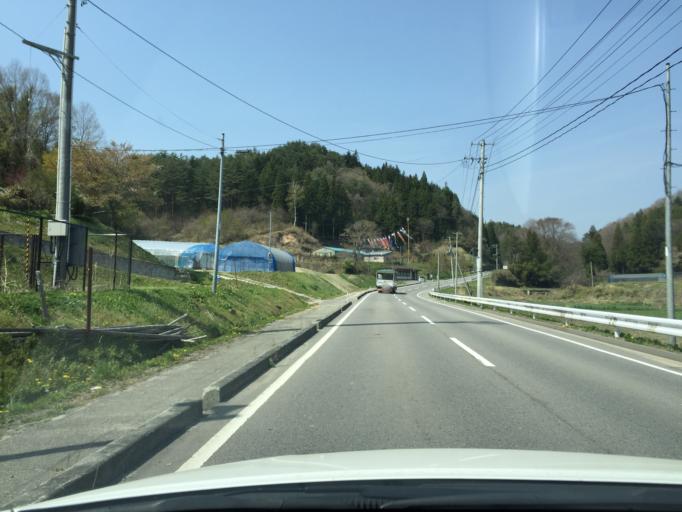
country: JP
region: Fukushima
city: Funehikimachi-funehiki
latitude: 37.4461
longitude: 140.6705
